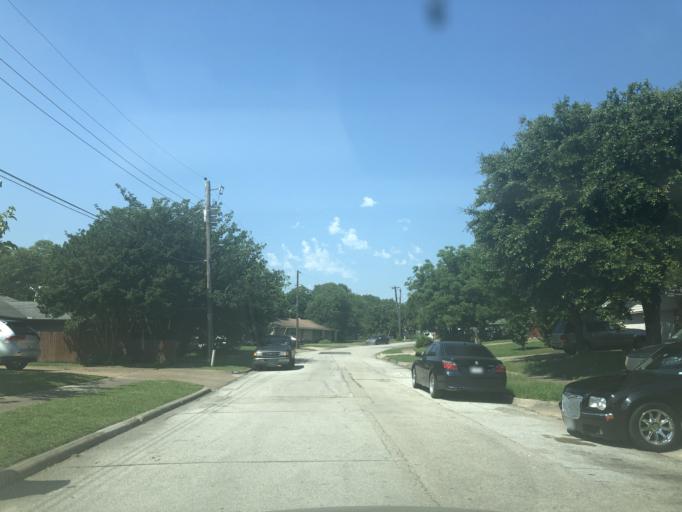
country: US
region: Texas
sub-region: Dallas County
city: Grand Prairie
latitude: 32.7225
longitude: -97.0061
